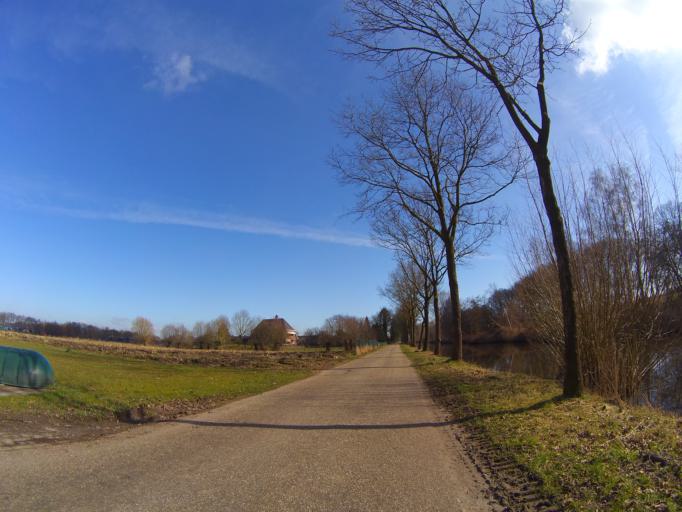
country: NL
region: Utrecht
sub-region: Gemeente Utrechtse Heuvelrug
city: Overberg
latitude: 52.0476
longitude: 5.5086
